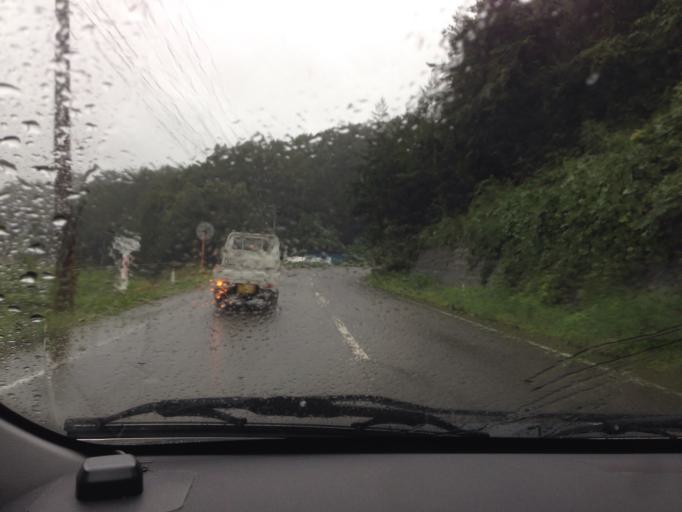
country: JP
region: Fukushima
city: Koriyama
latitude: 37.4371
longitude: 140.2628
